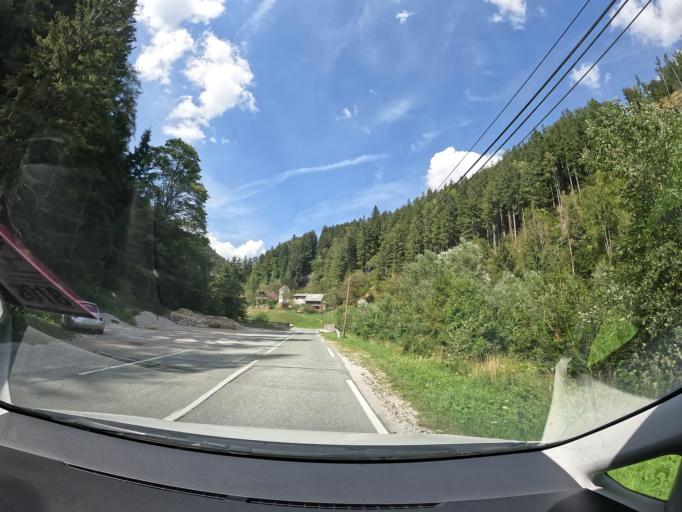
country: SI
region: Cerklje na Gorenjskem
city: Cerklje na Gorenjskem
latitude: 46.3247
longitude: 14.4915
